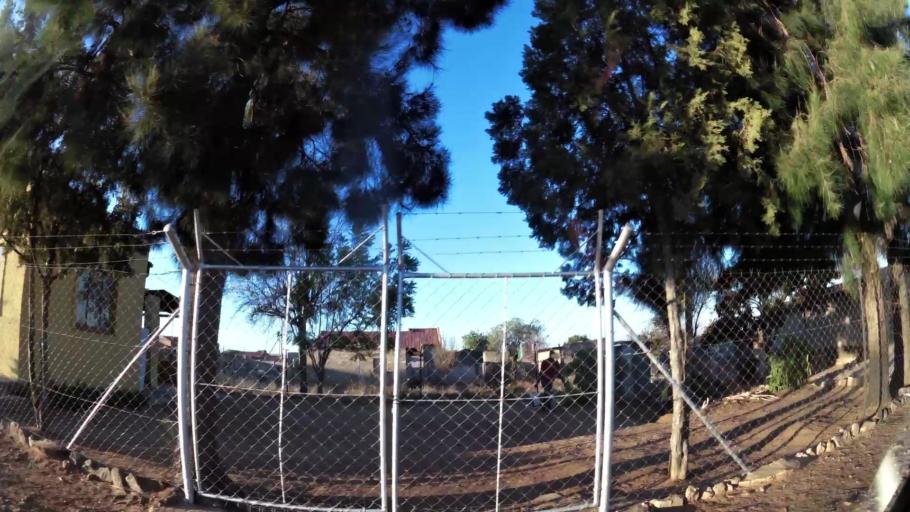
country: ZA
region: Limpopo
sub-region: Capricorn District Municipality
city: Polokwane
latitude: -23.8516
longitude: 29.3516
